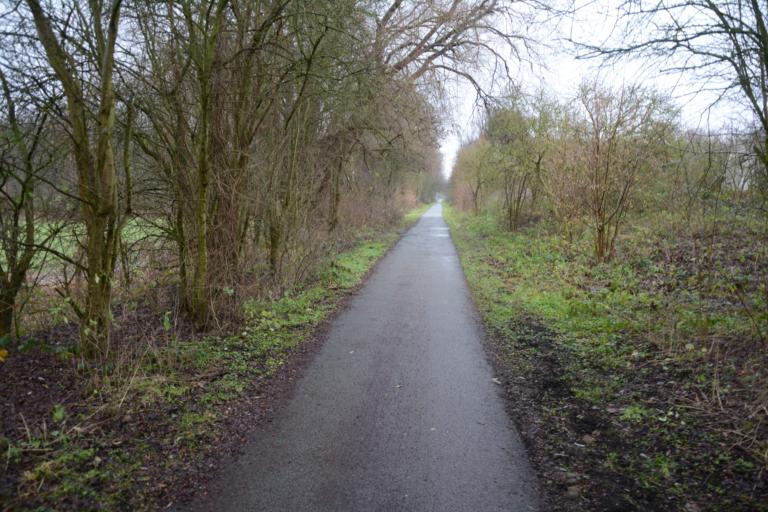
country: BE
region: Flanders
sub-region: Provincie Oost-Vlaanderen
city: Lebbeke
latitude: 50.9639
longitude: 4.1349
